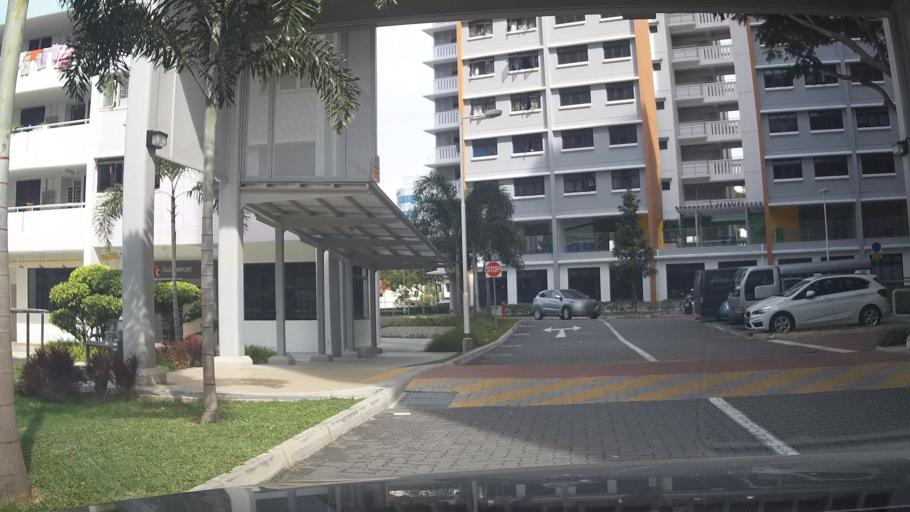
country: SG
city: Singapore
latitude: 1.3101
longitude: 103.8851
